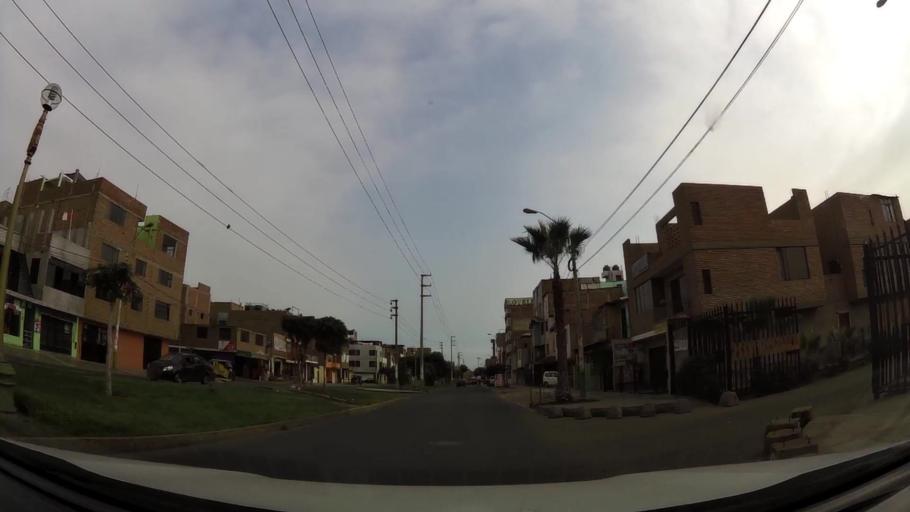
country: PE
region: Callao
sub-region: Callao
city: Callao
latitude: -12.0213
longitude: -77.0972
